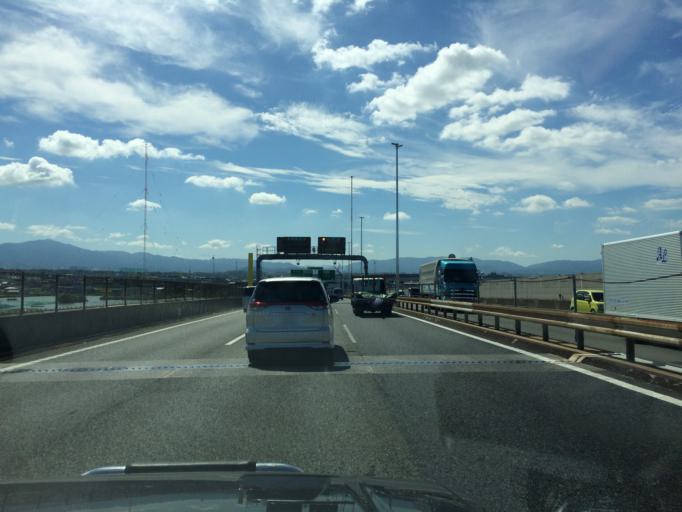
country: JP
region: Osaka
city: Matsubara
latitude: 34.5597
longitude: 135.5659
